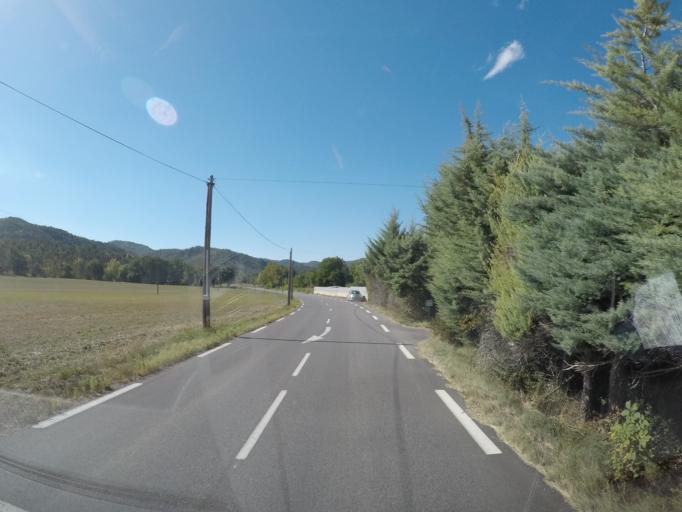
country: FR
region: Provence-Alpes-Cote d'Azur
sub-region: Departement des Alpes-de-Haute-Provence
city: Mallemoisson
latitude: 44.0460
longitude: 6.1611
